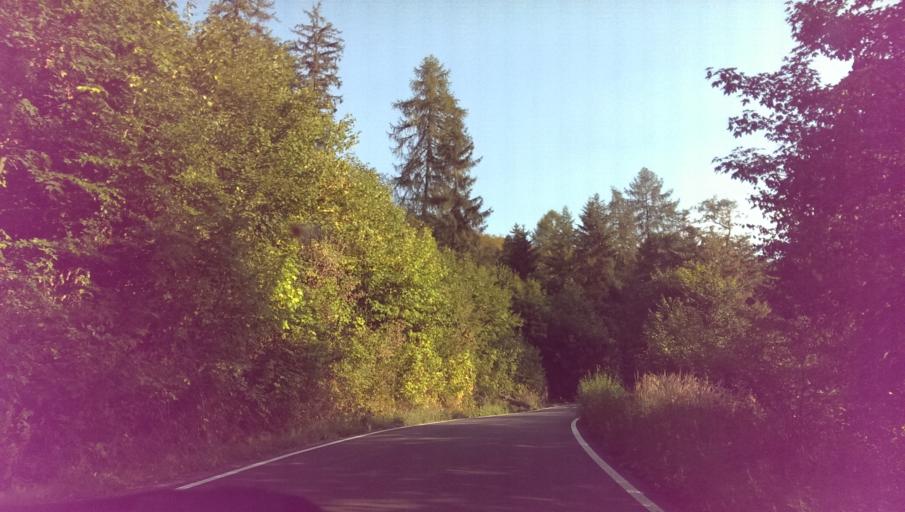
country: CZ
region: Zlin
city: Korycany
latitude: 49.0874
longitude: 17.2100
